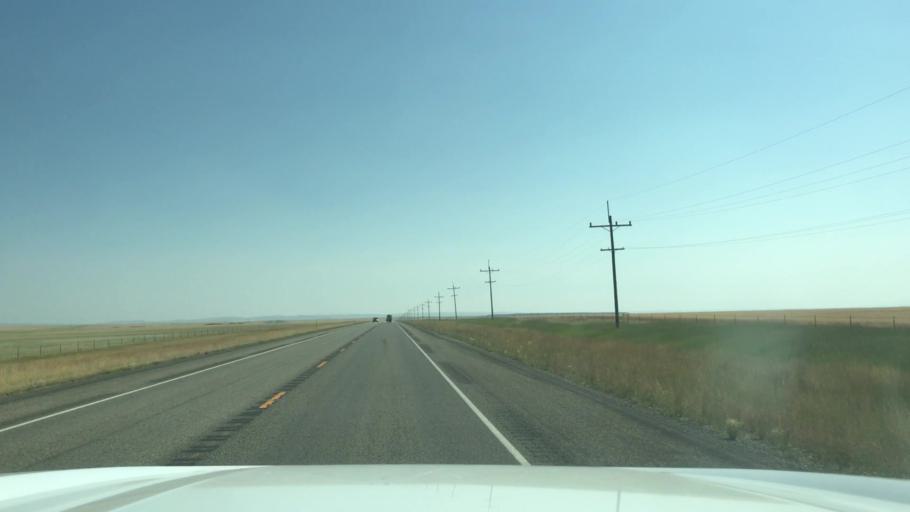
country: US
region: Montana
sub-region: Wheatland County
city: Harlowton
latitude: 46.5110
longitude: -109.7662
